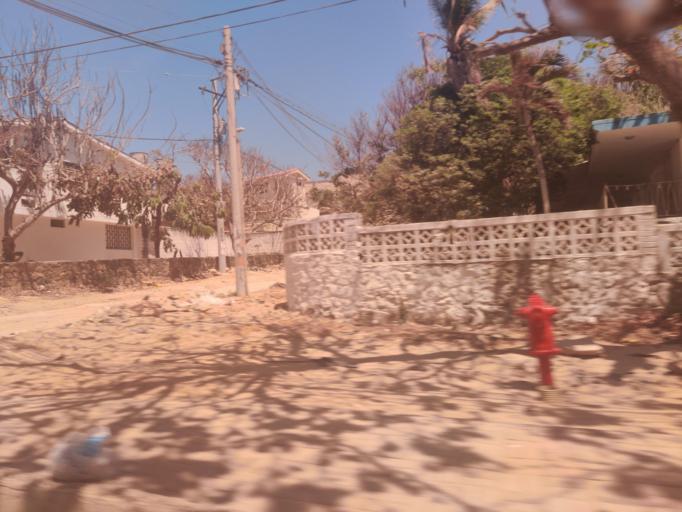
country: CO
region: Atlantico
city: Puerto Colombia
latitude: 11.0053
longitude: -74.9515
